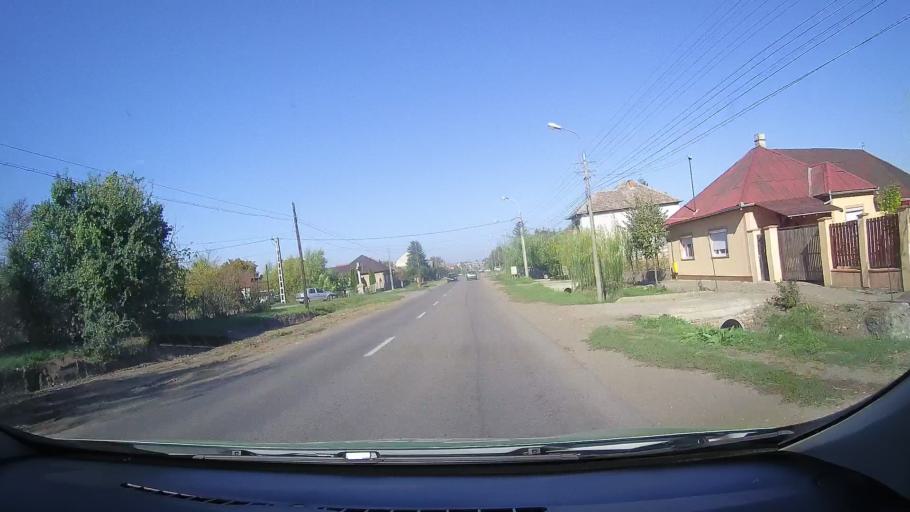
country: RO
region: Satu Mare
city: Carei
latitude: 47.6760
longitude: 22.4782
